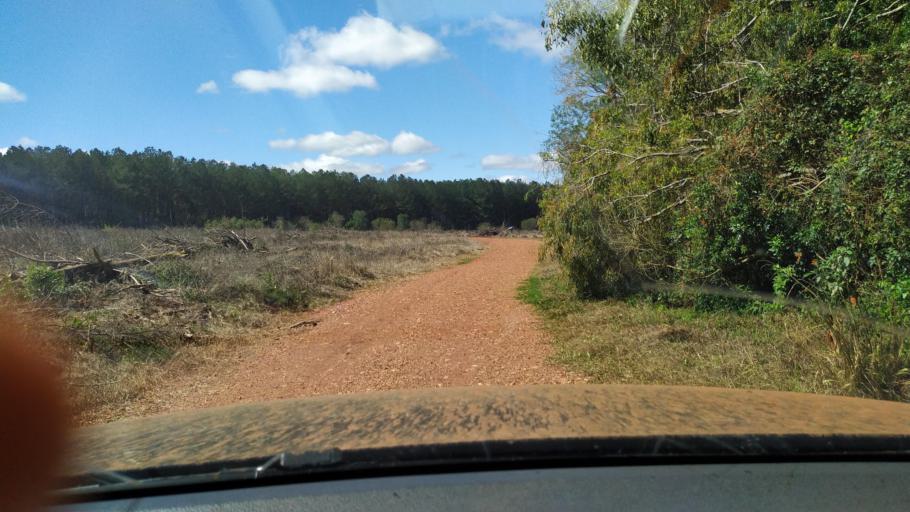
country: AR
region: Corrientes
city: Gobernador Ingeniero Valentin Virasoro
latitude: -28.2901
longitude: -56.0462
